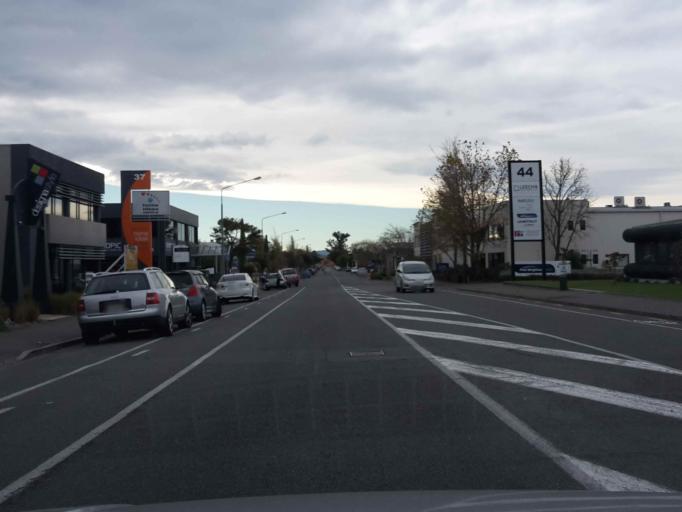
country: NZ
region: Canterbury
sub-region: Christchurch City
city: Christchurch
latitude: -43.5352
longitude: 172.6069
